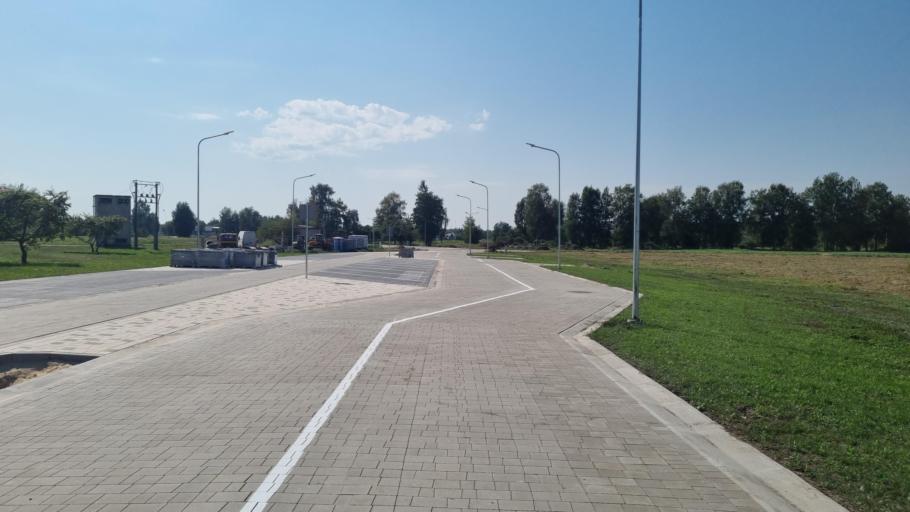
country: LV
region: Marupe
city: Marupe
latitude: 56.8830
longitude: 24.0646
